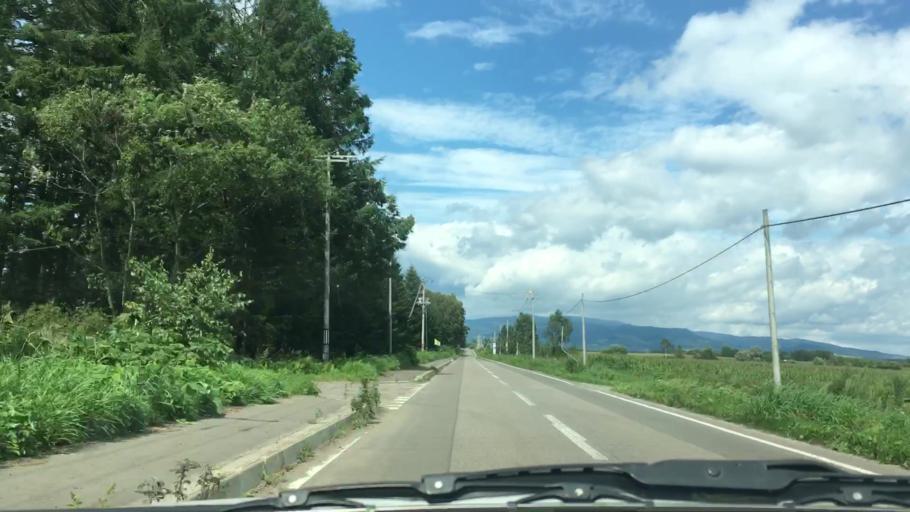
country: JP
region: Hokkaido
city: Otofuke
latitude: 43.2694
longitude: 143.3865
